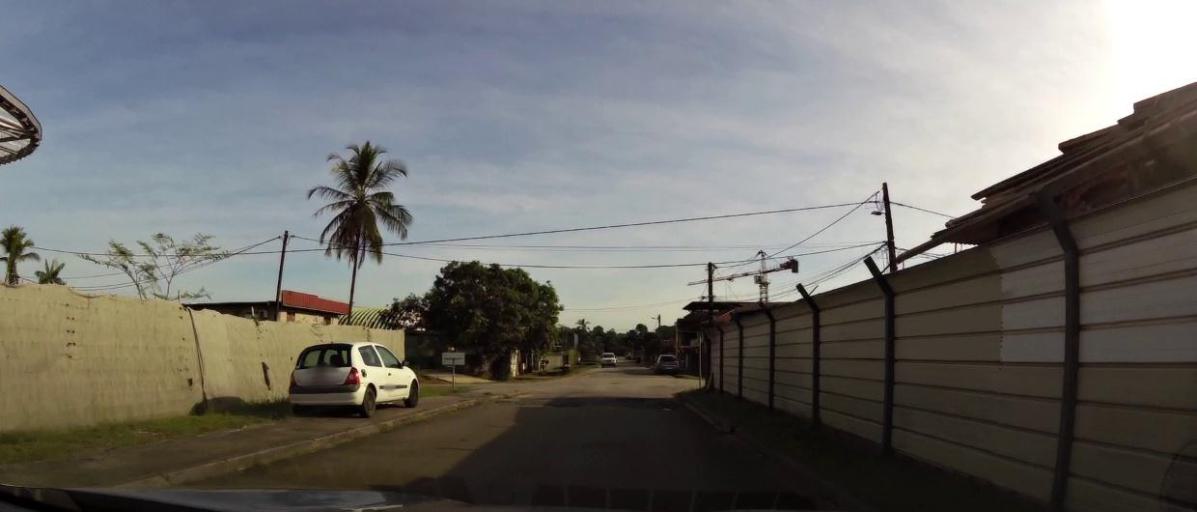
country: GF
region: Guyane
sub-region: Guyane
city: Cayenne
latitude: 4.8923
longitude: -52.3365
